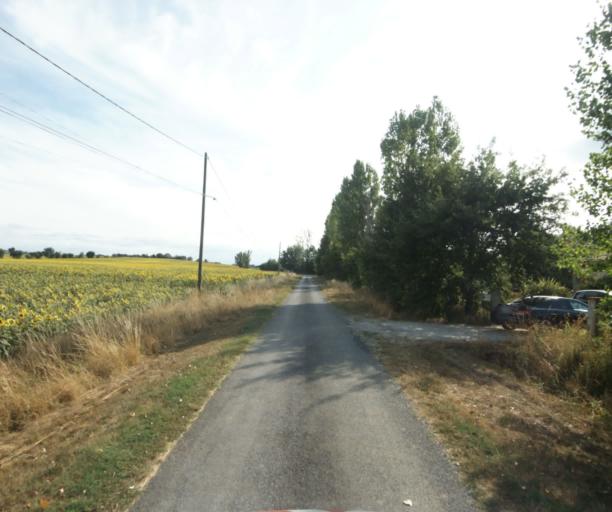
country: FR
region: Midi-Pyrenees
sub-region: Departement du Tarn
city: Puylaurens
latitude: 43.5179
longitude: 1.9999
